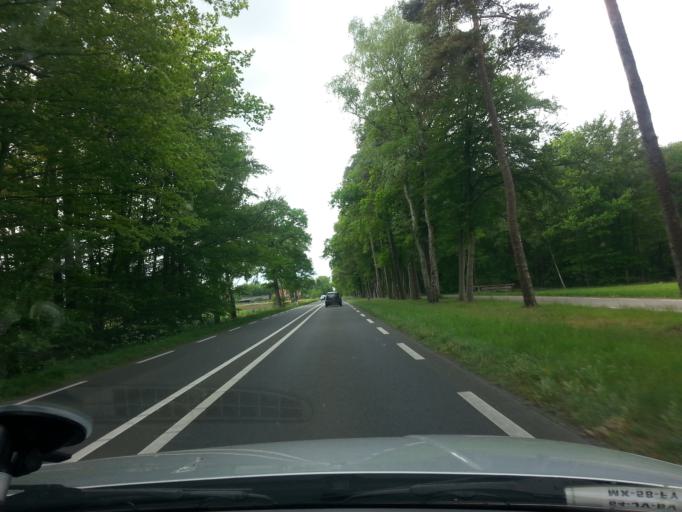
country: NL
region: Overijssel
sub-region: Gemeente Oldenzaal
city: Oldenzaal
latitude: 52.3407
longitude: 6.9632
